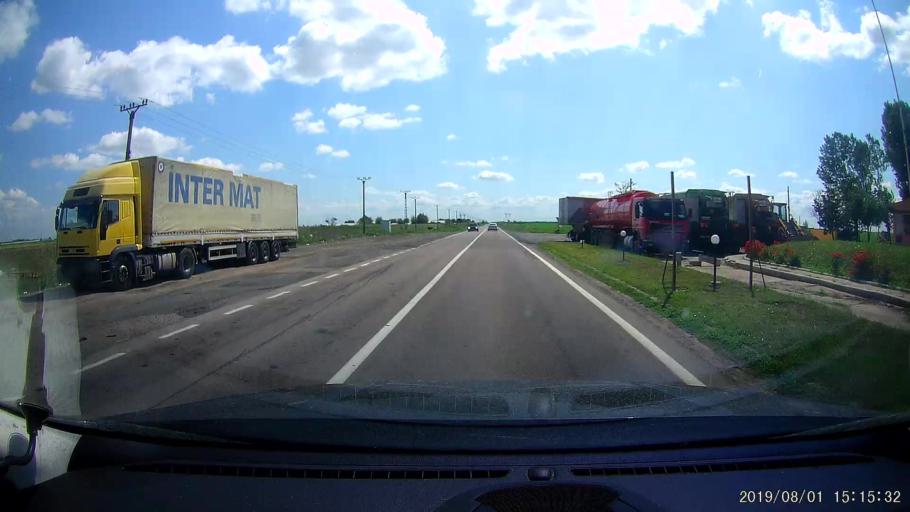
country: RO
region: Braila
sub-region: Comuna Tichilesti
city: Tichilesti
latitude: 45.1627
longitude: 27.8668
